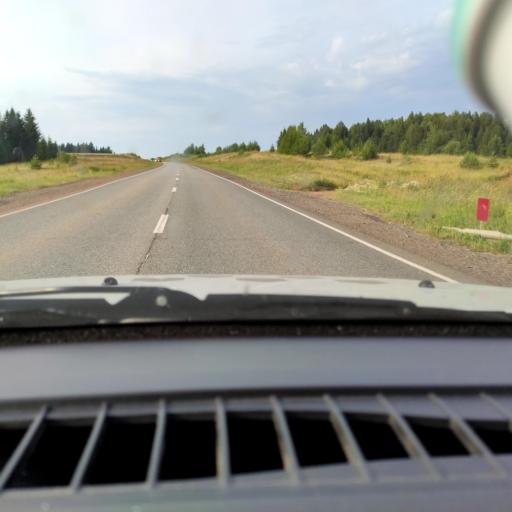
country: RU
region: Udmurtiya
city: Balezino
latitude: 57.8144
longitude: 52.9742
